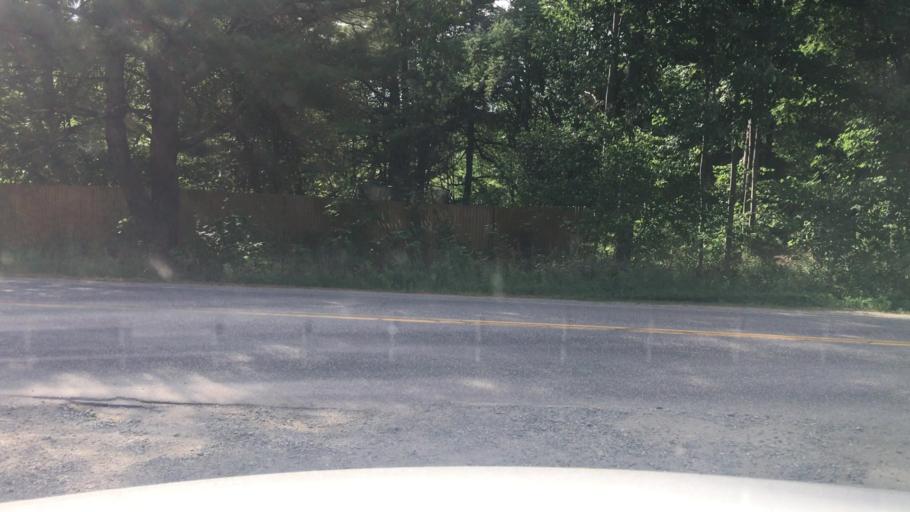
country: US
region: Maine
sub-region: Franklin County
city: Wilton
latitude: 44.5973
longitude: -70.2193
